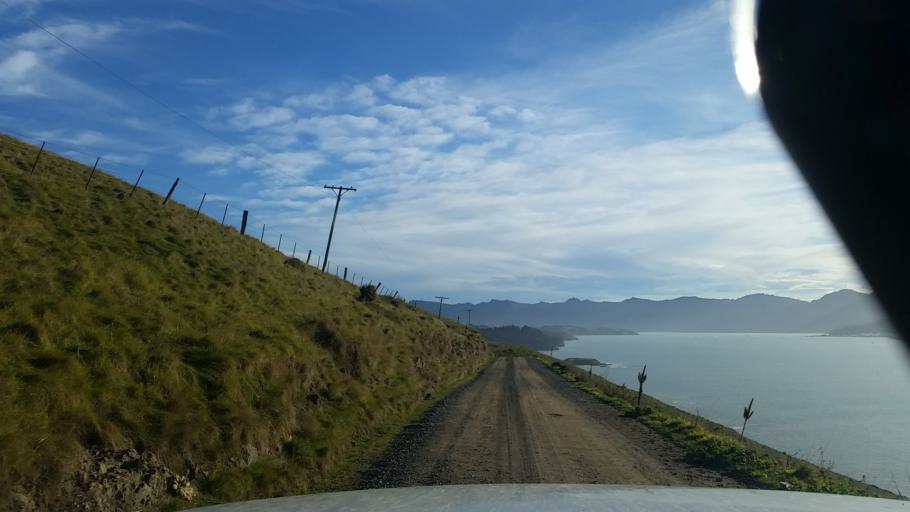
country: NZ
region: Canterbury
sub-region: Christchurch City
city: Christchurch
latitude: -43.6177
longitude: 172.7741
